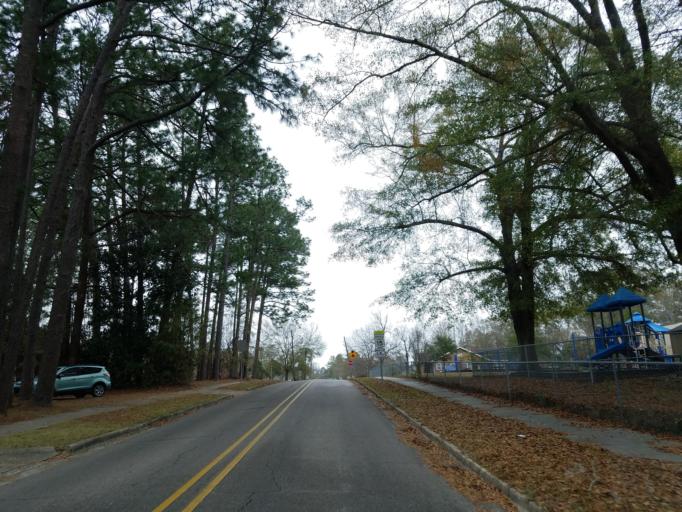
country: US
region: Mississippi
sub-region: Forrest County
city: Hattiesburg
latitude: 31.3219
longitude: -89.3228
